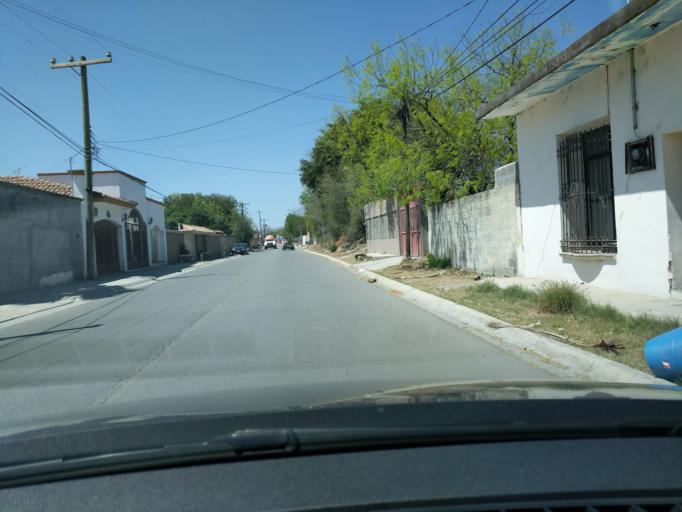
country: MX
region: Nuevo Leon
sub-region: Apodaca
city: Artemio Trevino
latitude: 25.8129
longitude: -100.1416
